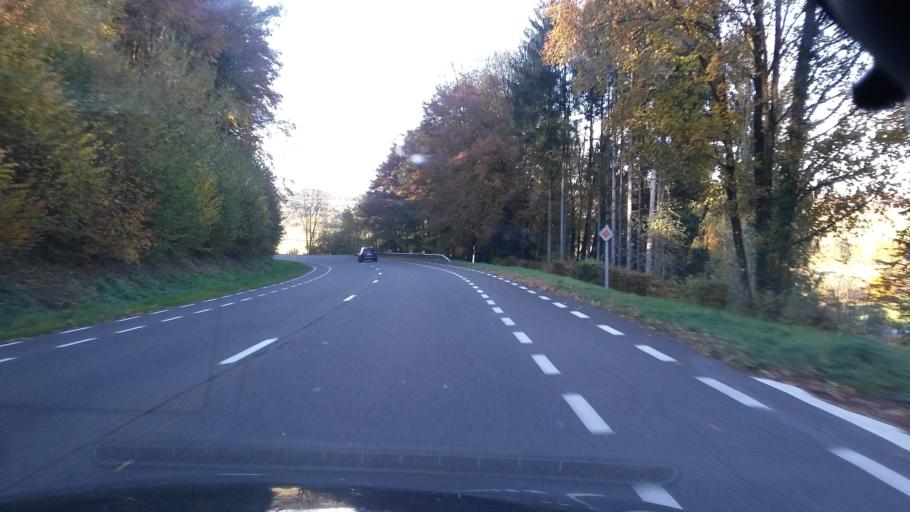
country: BE
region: Wallonia
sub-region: Province du Luxembourg
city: Florenville
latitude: 49.7090
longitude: 5.2590
